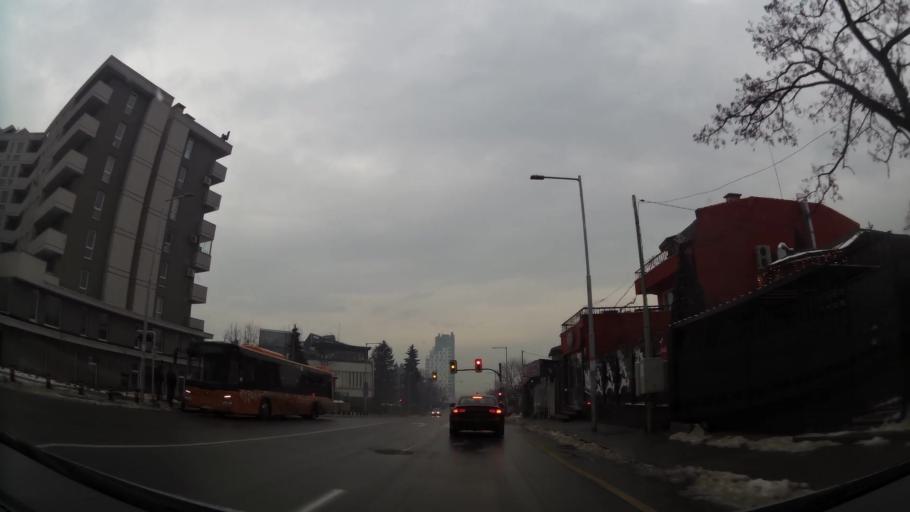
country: BG
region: Sofia-Capital
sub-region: Stolichna Obshtina
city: Sofia
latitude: 42.6765
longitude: 23.2533
